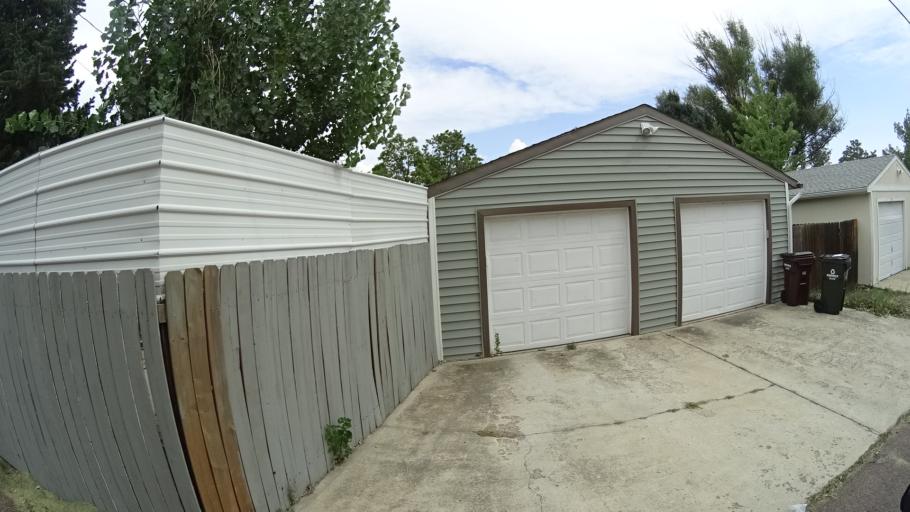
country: US
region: Colorado
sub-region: El Paso County
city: Colorado Springs
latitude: 38.8630
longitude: -104.7923
